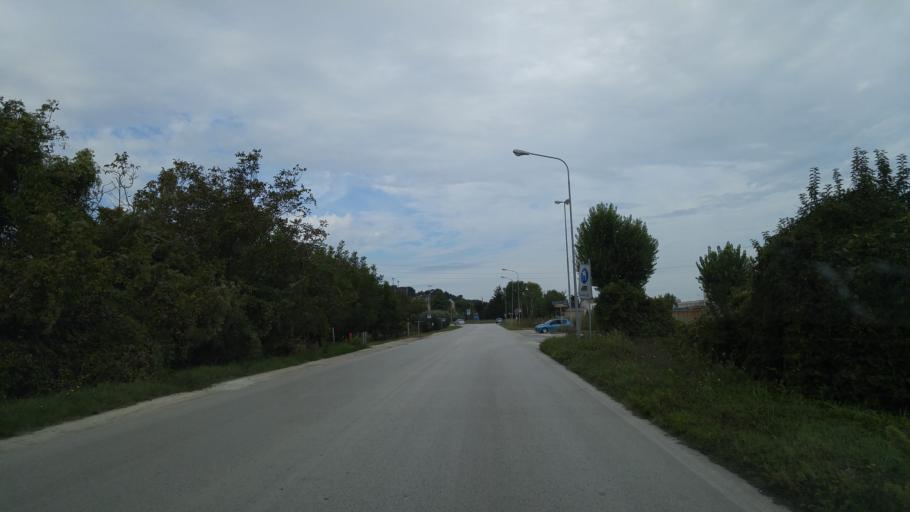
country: IT
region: The Marches
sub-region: Provincia di Pesaro e Urbino
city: Rosciano
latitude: 43.8144
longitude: 13.0009
